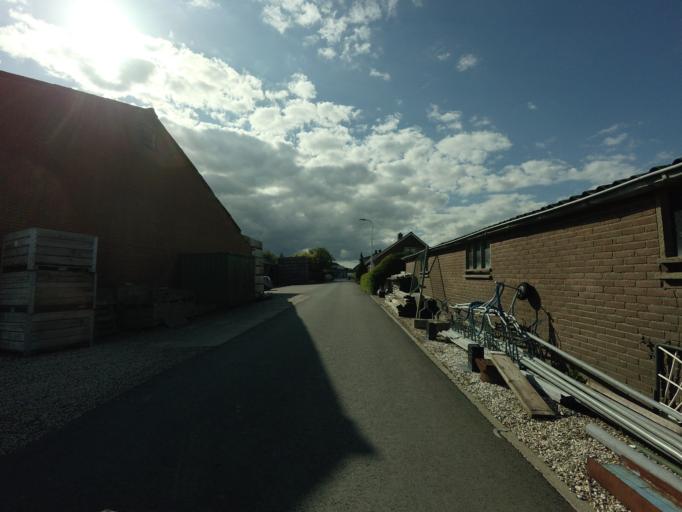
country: NL
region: Utrecht
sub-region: Gemeente Lopik
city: Lopik
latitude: 51.9594
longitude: 4.9819
